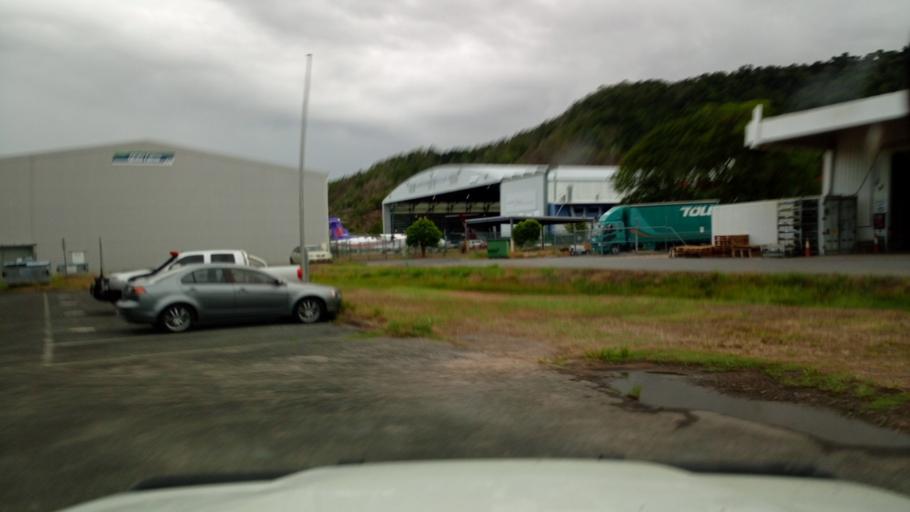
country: AU
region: Queensland
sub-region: Cairns
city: Cairns
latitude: -16.8821
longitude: 145.7488
